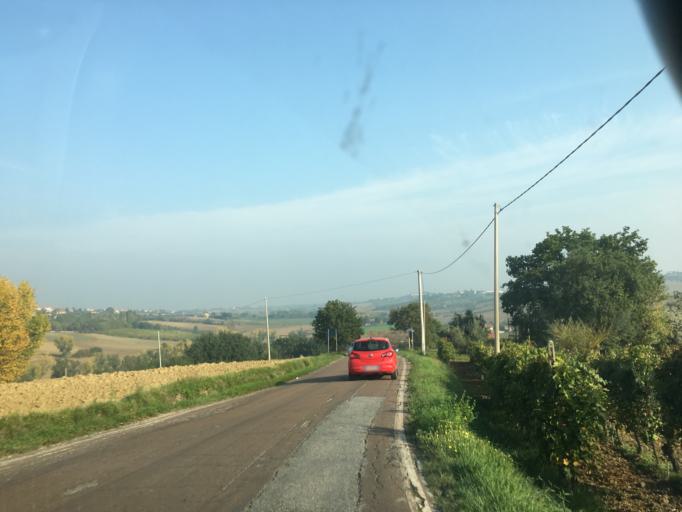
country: IT
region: Emilia-Romagna
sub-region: Provincia di Rimini
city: Coriano
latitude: 43.9512
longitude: 12.6118
